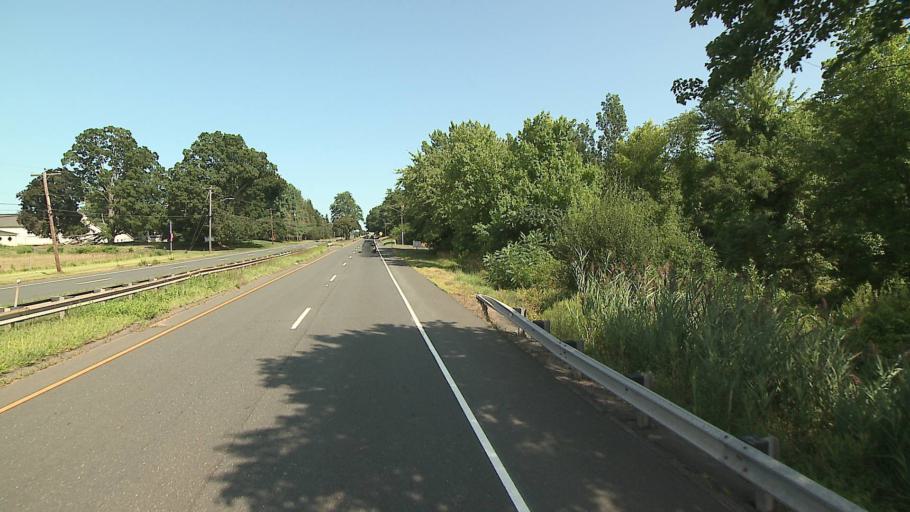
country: US
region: Connecticut
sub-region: Hartford County
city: Windsor
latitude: 41.8635
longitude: -72.6040
